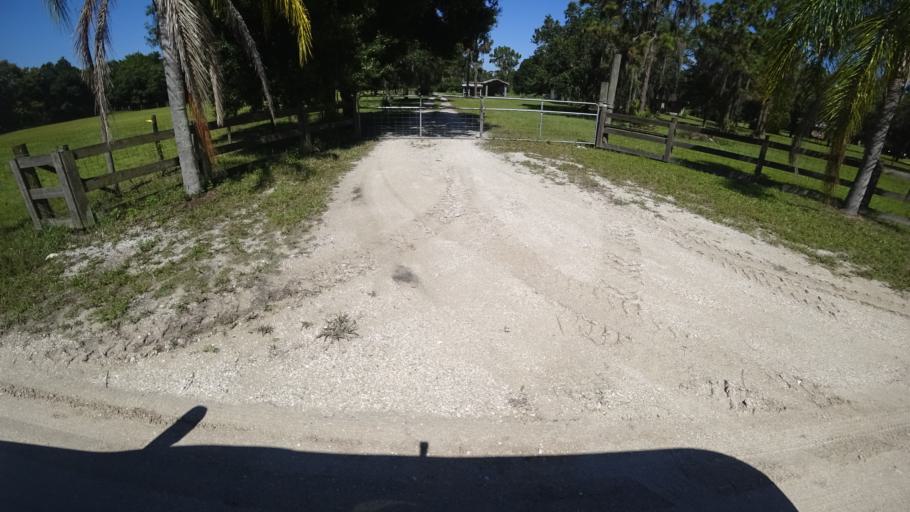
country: US
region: Florida
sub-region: Sarasota County
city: The Meadows
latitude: 27.4472
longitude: -82.2952
